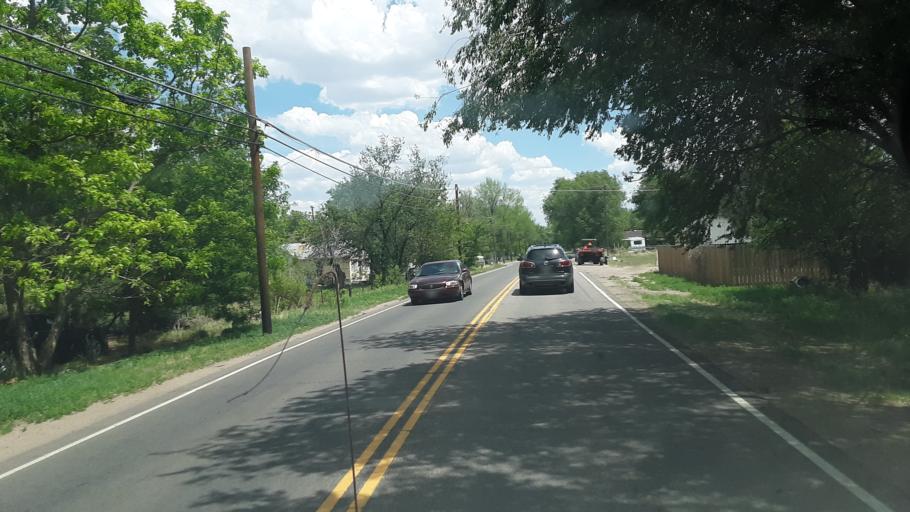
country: US
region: Colorado
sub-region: Fremont County
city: Florence
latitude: 38.4016
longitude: -105.1360
